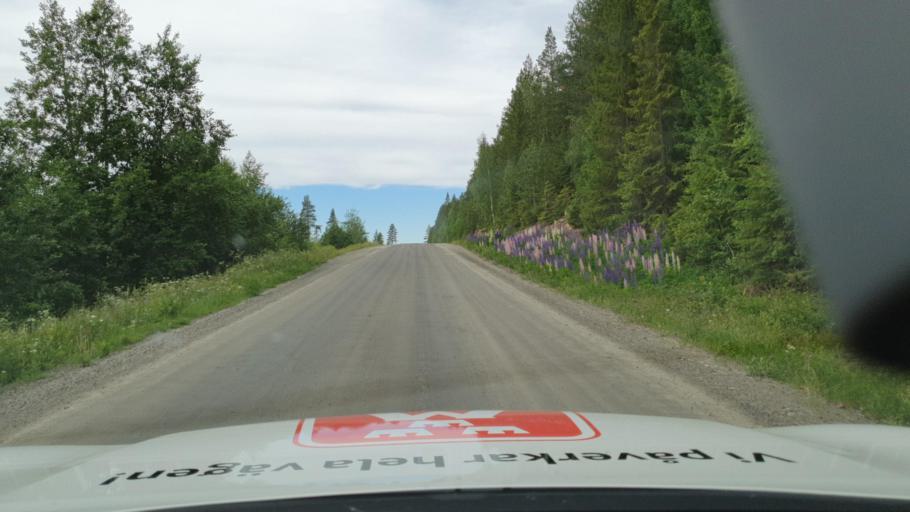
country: SE
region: Vaesterbotten
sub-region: Skelleftea Kommun
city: Burtraesk
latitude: 64.3725
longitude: 20.3722
